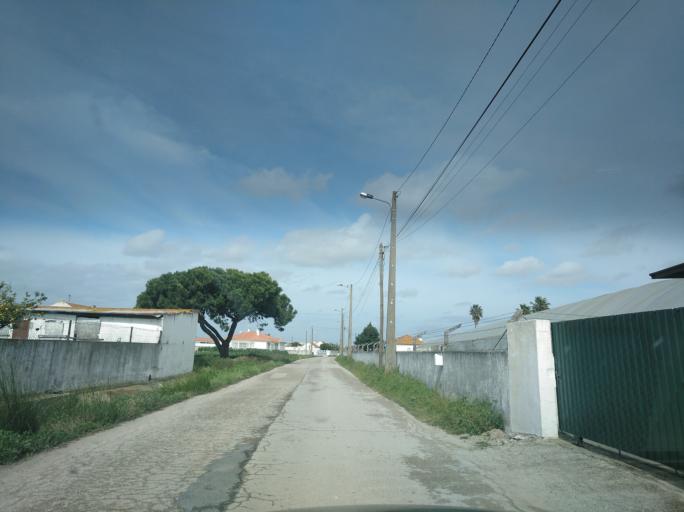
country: PT
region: Setubal
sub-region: Palmela
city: Pinhal Novo
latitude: 38.6659
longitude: -8.9184
